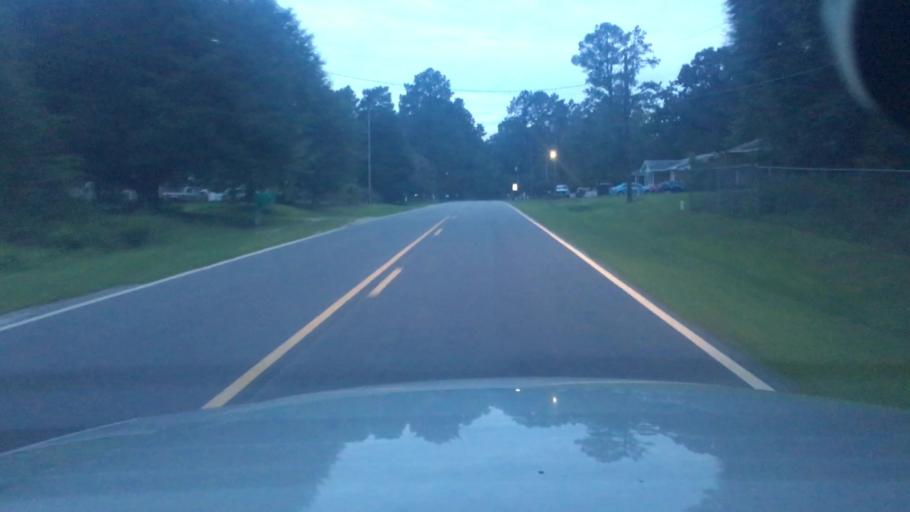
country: US
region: North Carolina
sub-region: Cumberland County
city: Hope Mills
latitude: 34.9595
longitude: -78.9284
